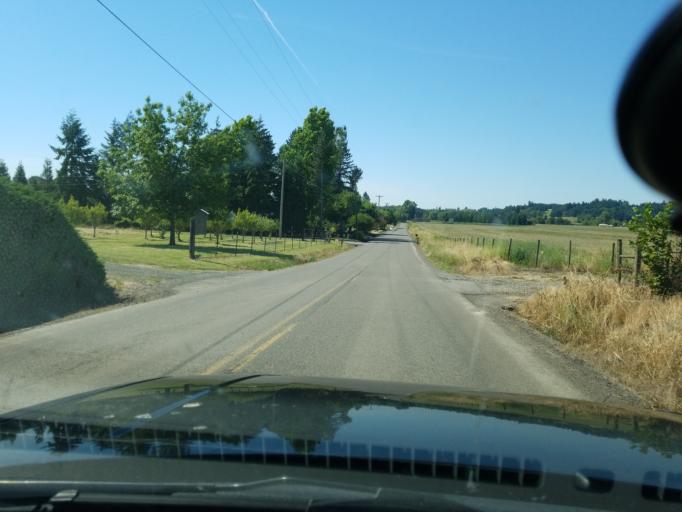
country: US
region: Oregon
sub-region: Yamhill County
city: McMinnville
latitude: 45.2382
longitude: -123.2309
